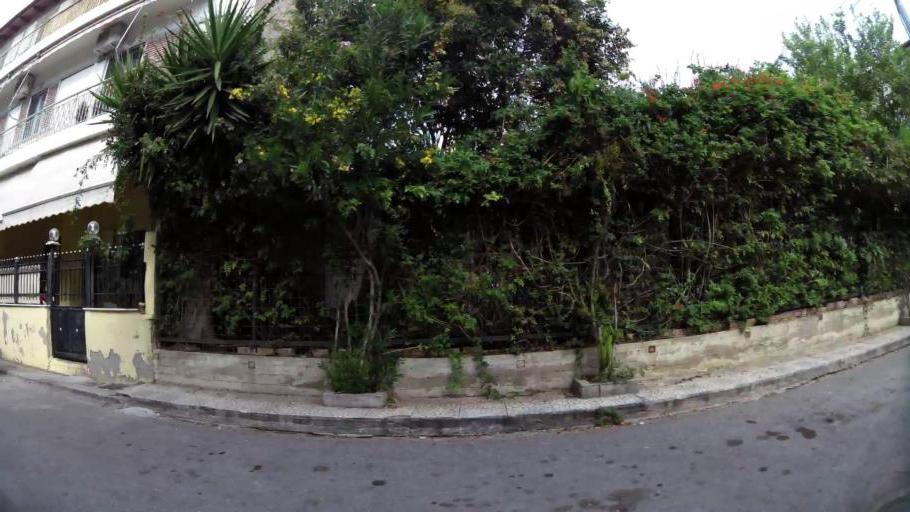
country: GR
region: Attica
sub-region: Nomarchia Athinas
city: Petroupolis
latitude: 38.0267
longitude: 23.6785
